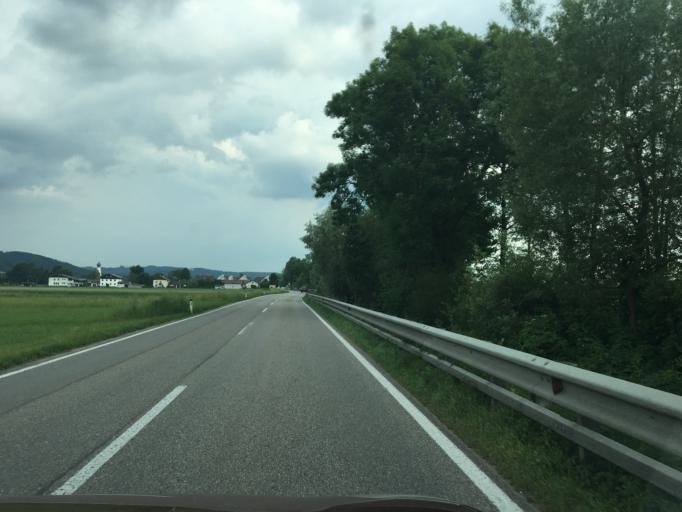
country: AT
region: Upper Austria
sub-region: Politischer Bezirk Braunau am Inn
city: Altheim
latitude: 48.1251
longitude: 13.1488
